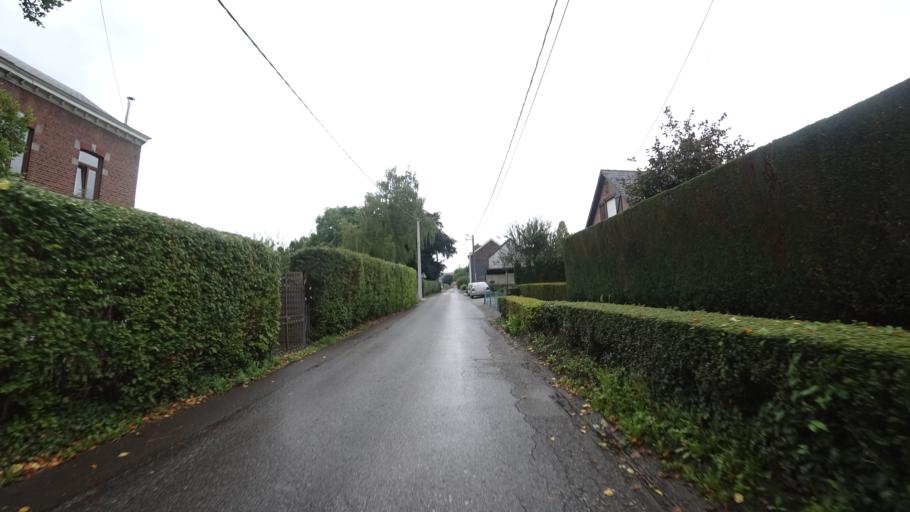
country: BE
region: Wallonia
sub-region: Province de Namur
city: Namur
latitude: 50.4611
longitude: 4.8198
